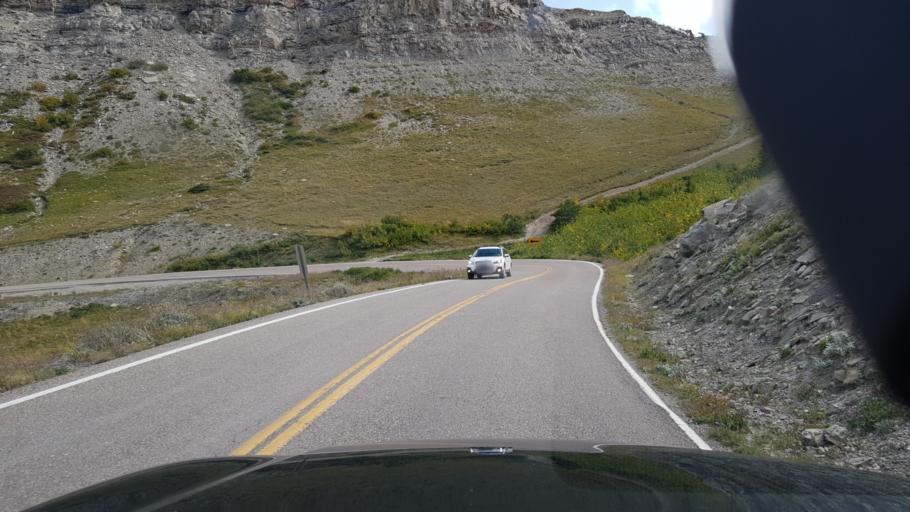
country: US
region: Montana
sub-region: Glacier County
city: South Browning
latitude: 48.5411
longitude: -113.2969
